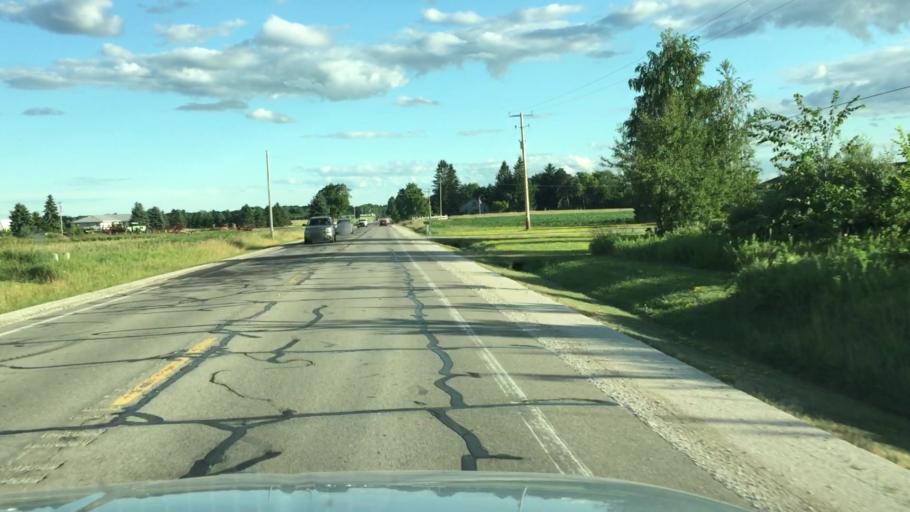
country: US
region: Michigan
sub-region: Saint Clair County
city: Yale
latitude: 43.0840
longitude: -82.7659
